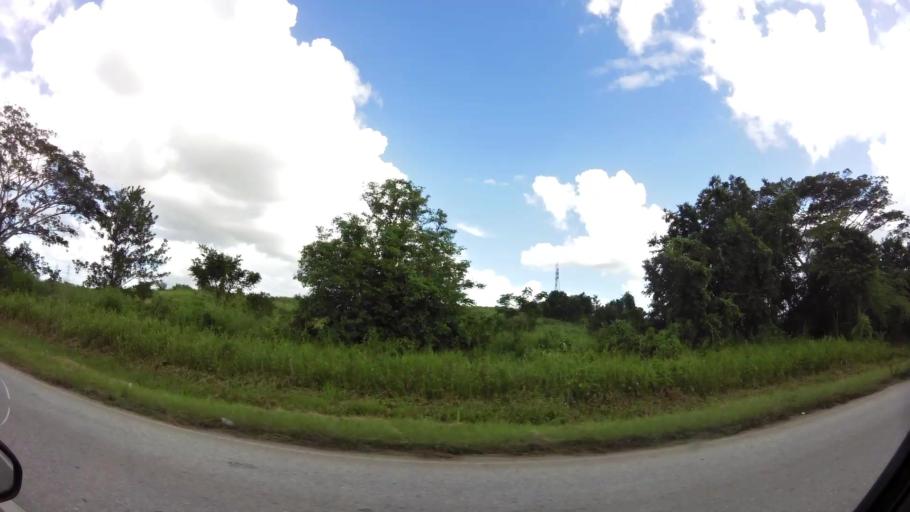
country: TT
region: Penal/Debe
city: Debe
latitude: 10.2294
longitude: -61.4351
